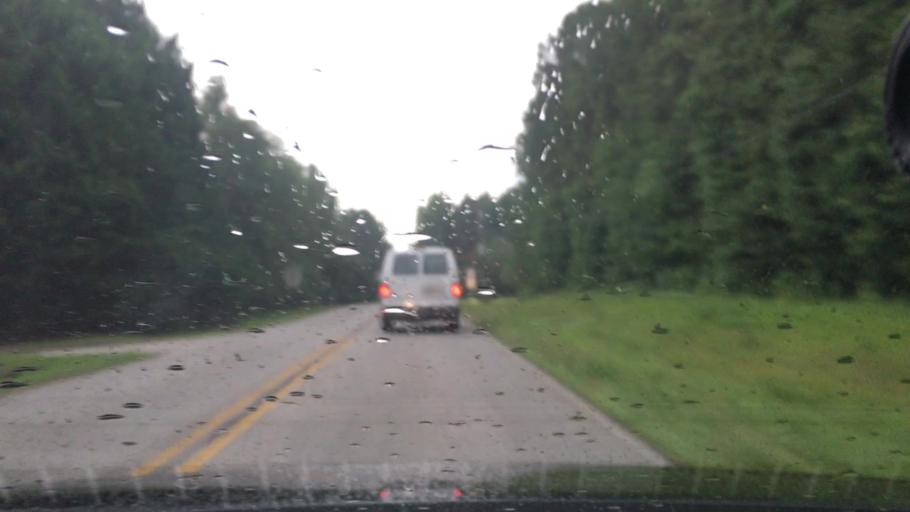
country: US
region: Georgia
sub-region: Coweta County
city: East Newnan
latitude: 33.3895
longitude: -84.7017
